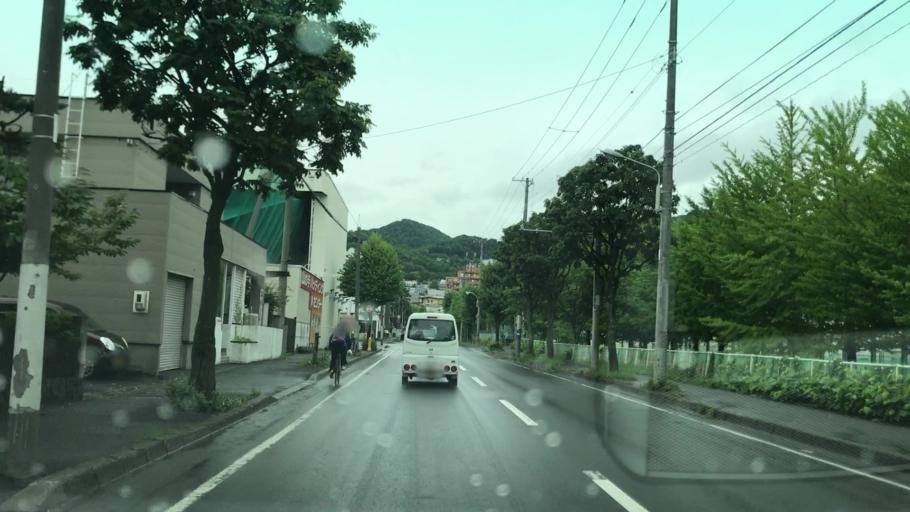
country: JP
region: Hokkaido
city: Sapporo
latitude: 43.0623
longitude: 141.3021
